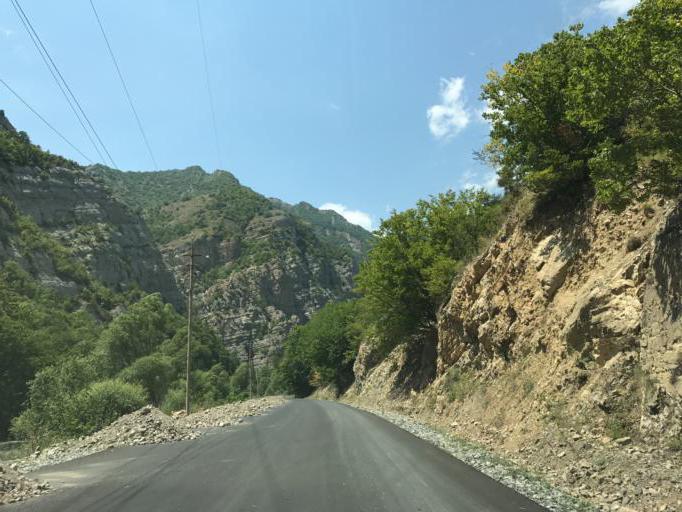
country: AZ
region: Kalbacar Rayonu
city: Kerbakhiar
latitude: 40.1600
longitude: 46.2169
